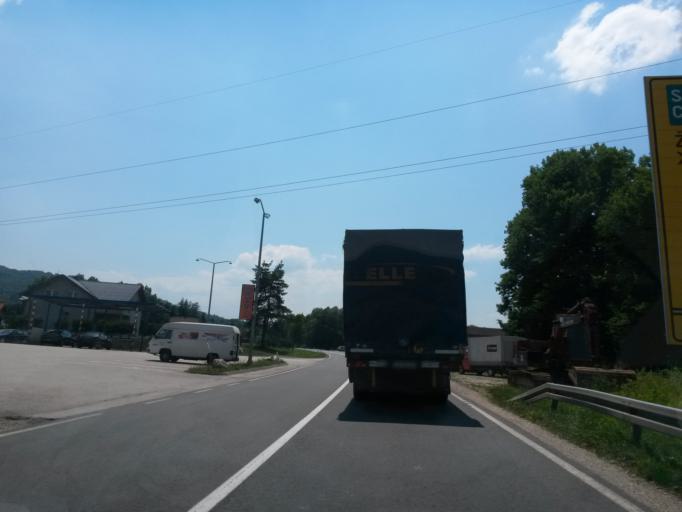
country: BA
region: Federation of Bosnia and Herzegovina
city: Lijesnica
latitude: 44.4807
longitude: 18.0682
